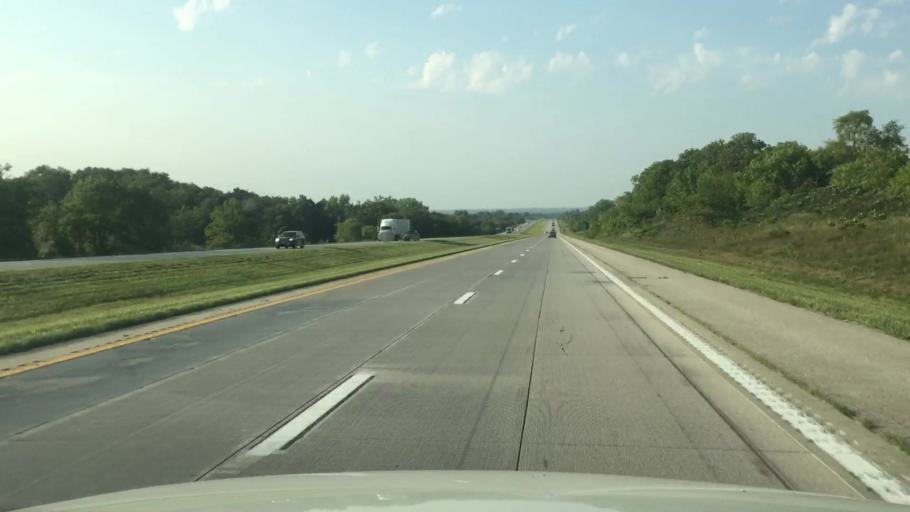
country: US
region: Missouri
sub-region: Daviess County
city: Gallatin
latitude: 39.9790
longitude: -94.0942
